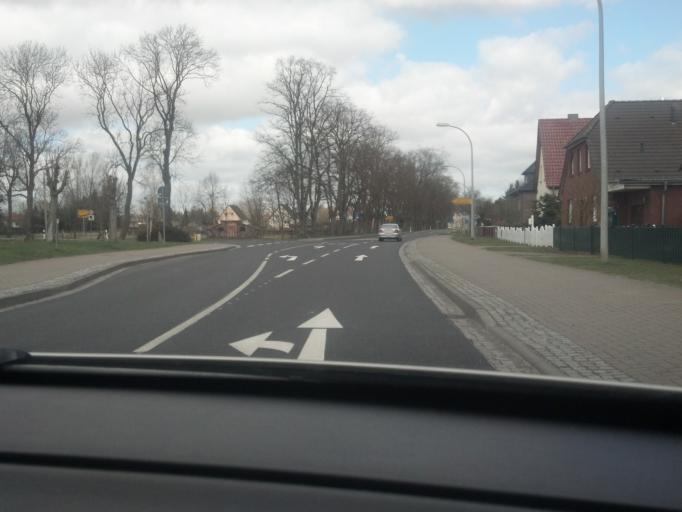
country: DE
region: Brandenburg
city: Gerdshagen
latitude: 53.3201
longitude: 12.2402
